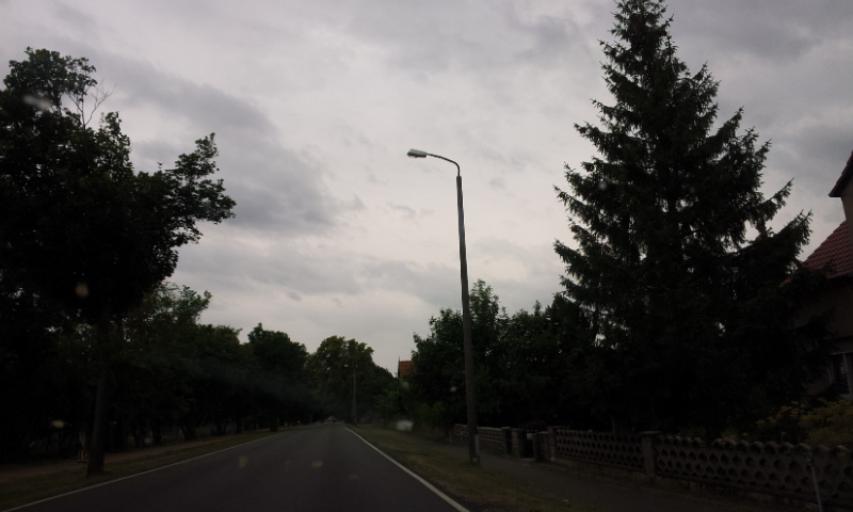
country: DE
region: Brandenburg
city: Niedergorsdorf
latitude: 52.0146
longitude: 12.9987
